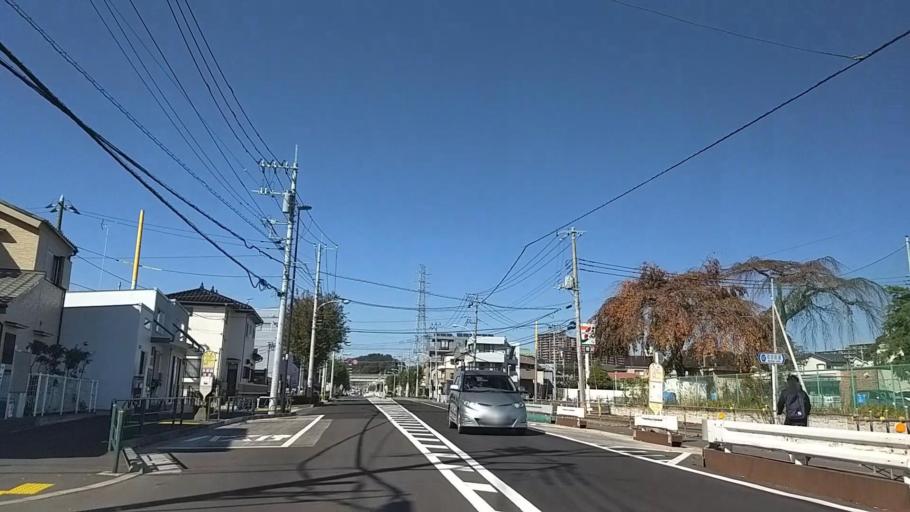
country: JP
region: Tokyo
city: Hachioji
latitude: 35.5970
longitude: 139.3683
